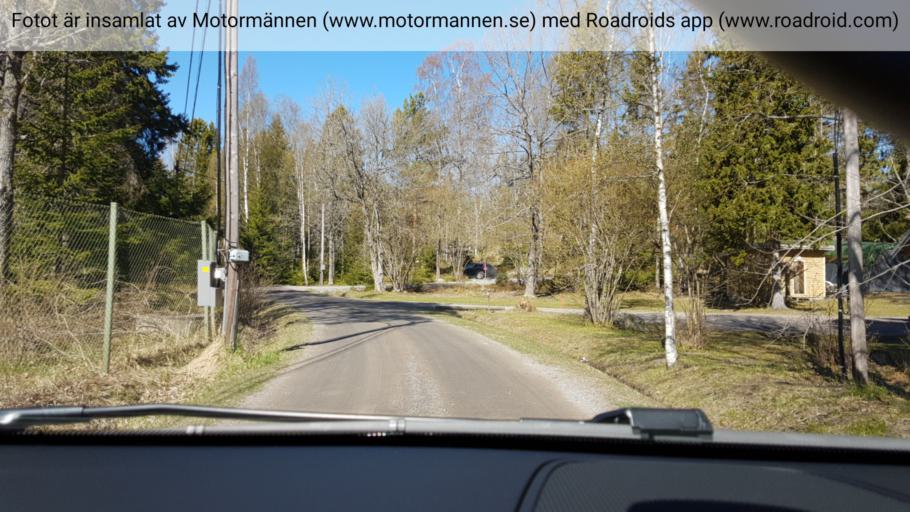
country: SE
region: Stockholm
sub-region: Varmdo Kommun
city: Hemmesta
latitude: 59.2928
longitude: 18.5560
